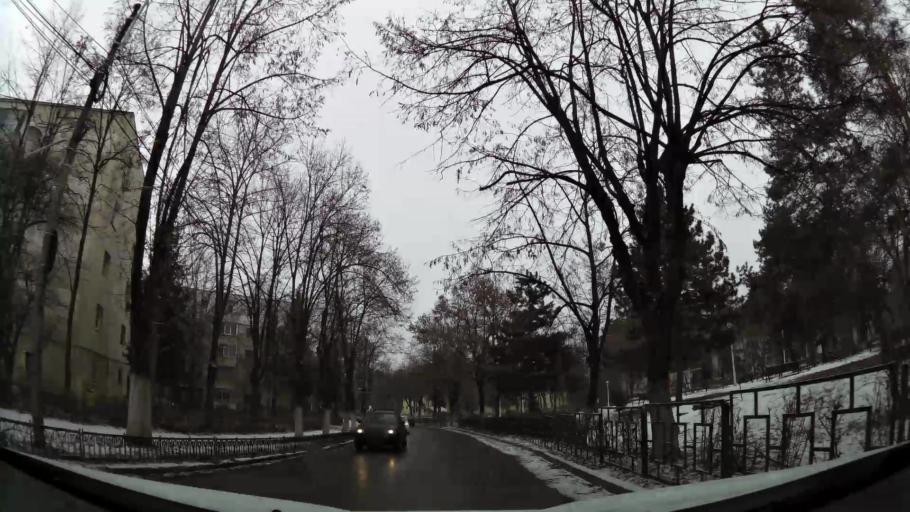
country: RO
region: Prahova
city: Ploiesti
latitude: 44.9603
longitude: 26.0042
